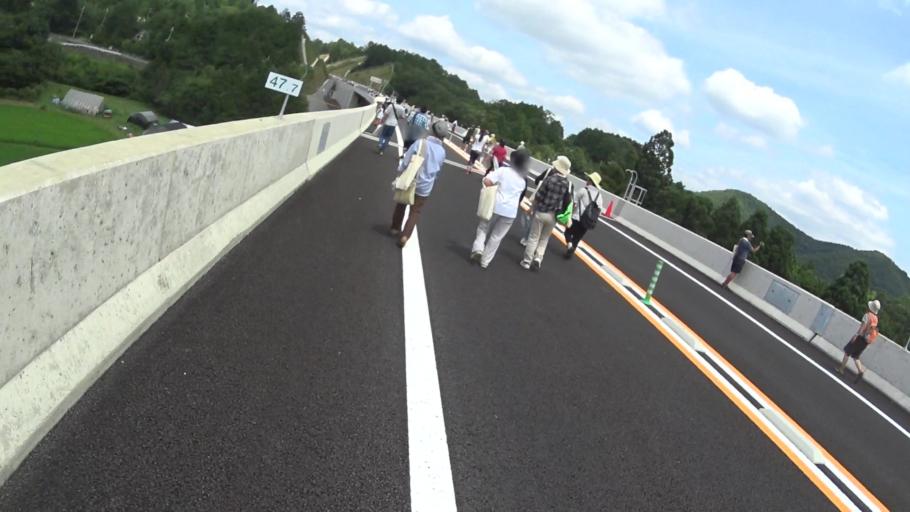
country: JP
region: Kyoto
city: Ayabe
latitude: 35.1656
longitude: 135.3846
